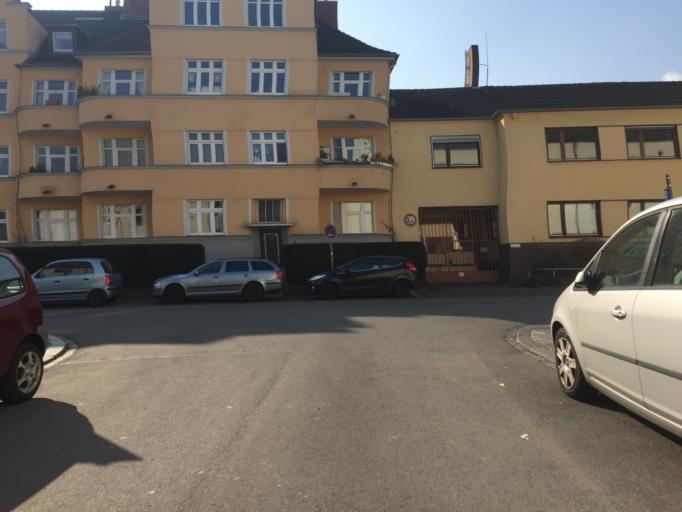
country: DE
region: North Rhine-Westphalia
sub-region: Regierungsbezirk Koln
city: Bonn
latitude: 50.7337
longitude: 7.0839
